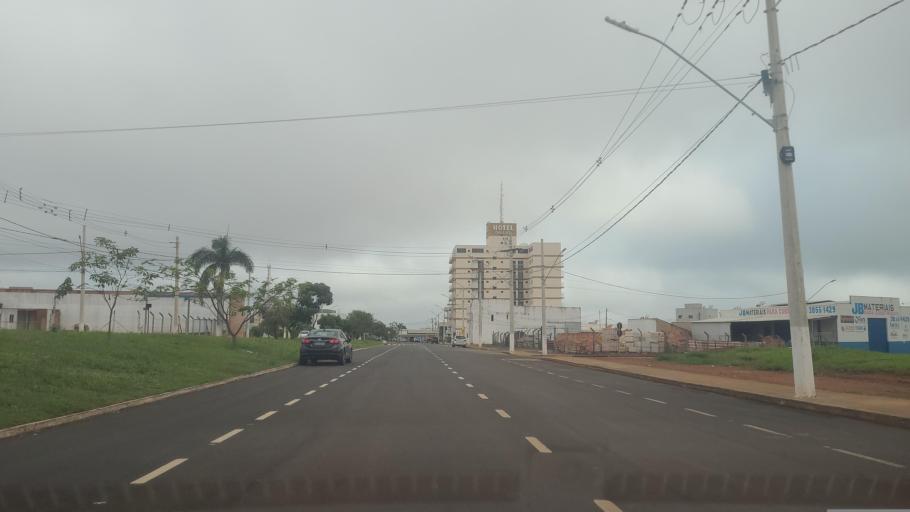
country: BR
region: Minas Gerais
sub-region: Sao Gotardo
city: Sao Gotardo
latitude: -19.2014
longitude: -46.2338
